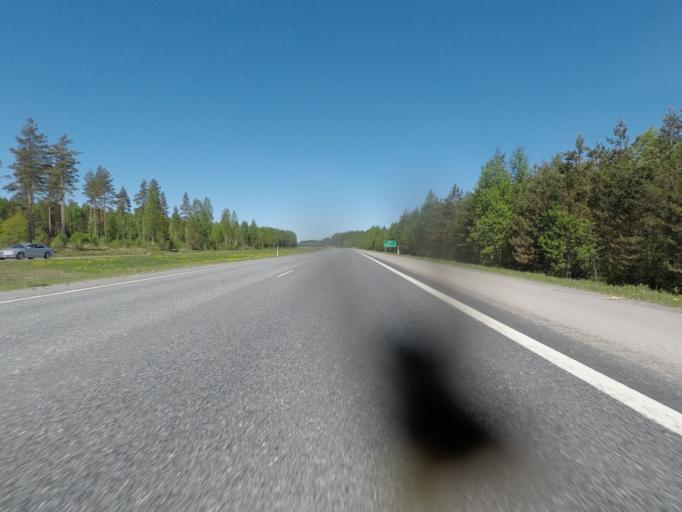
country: FI
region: Haeme
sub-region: Haemeenlinna
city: Haemeenlinna
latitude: 60.9373
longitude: 24.5153
